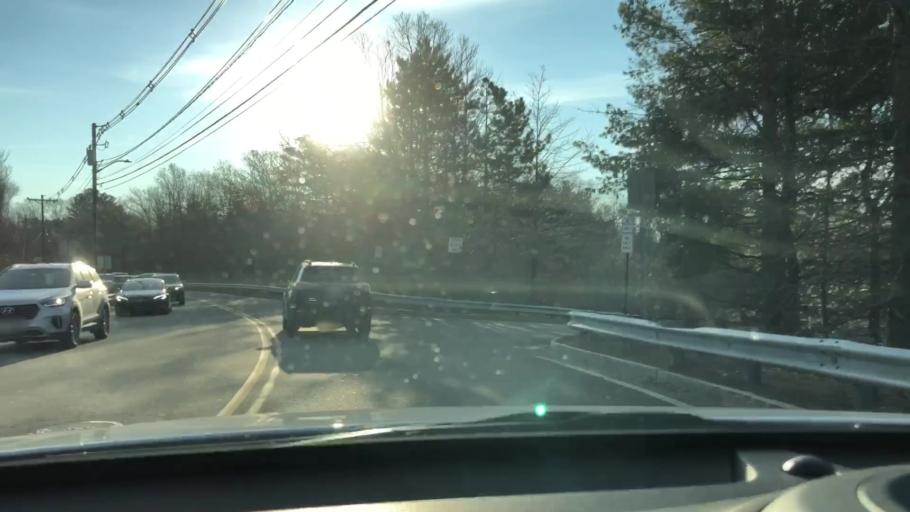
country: US
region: Massachusetts
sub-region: Plymouth County
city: Rockland
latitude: 42.1650
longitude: -70.8937
